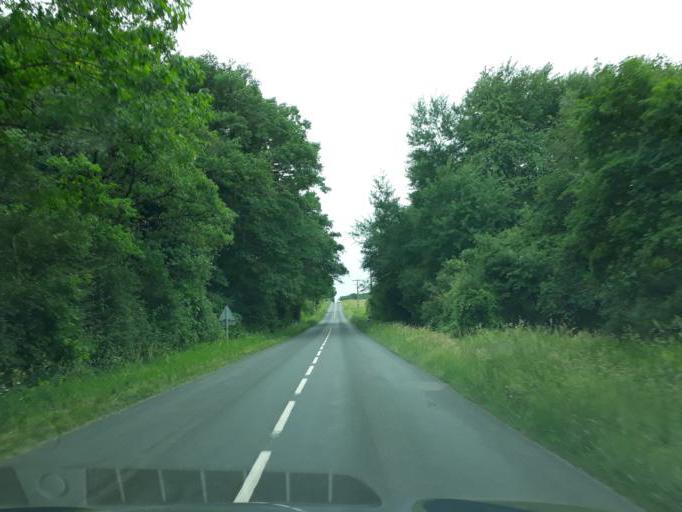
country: FR
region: Centre
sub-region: Departement du Loiret
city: Saint-Pere-sur-Loire
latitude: 47.7418
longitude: 2.3531
